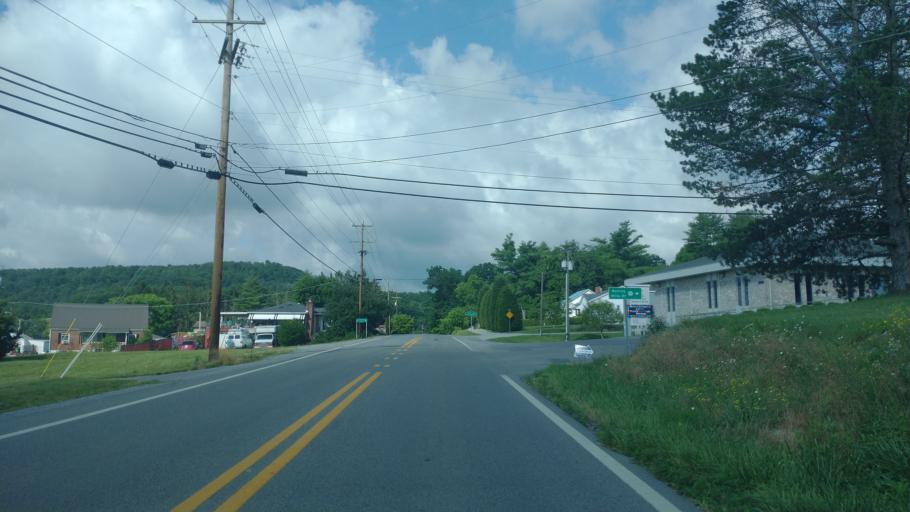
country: US
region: West Virginia
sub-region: Mercer County
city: Princeton
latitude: 37.3629
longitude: -81.1232
